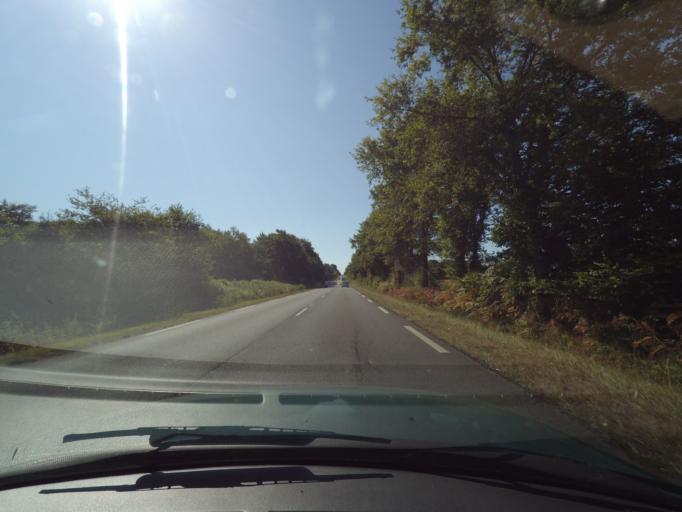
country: FR
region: Limousin
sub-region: Departement de la Haute-Vienne
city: Bussiere-Poitevine
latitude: 46.1960
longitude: 0.9251
